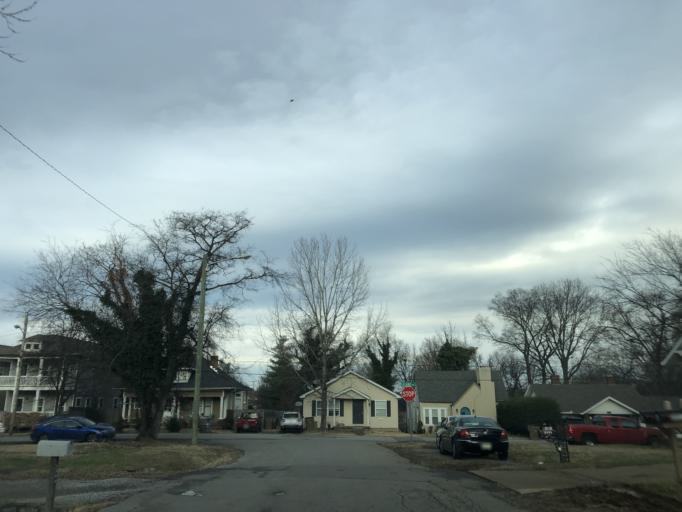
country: US
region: Tennessee
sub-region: Davidson County
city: Nashville
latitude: 36.2033
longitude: -86.7369
